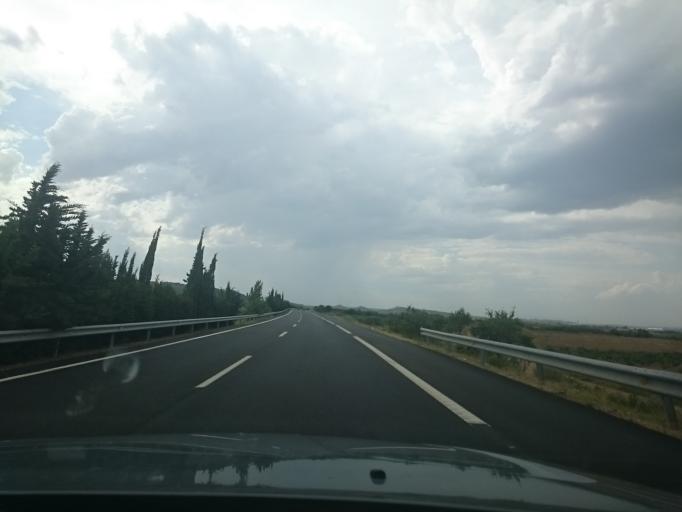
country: ES
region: La Rioja
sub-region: Provincia de La Rioja
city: Aldeanueva de Ebro
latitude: 42.2492
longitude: -1.9073
